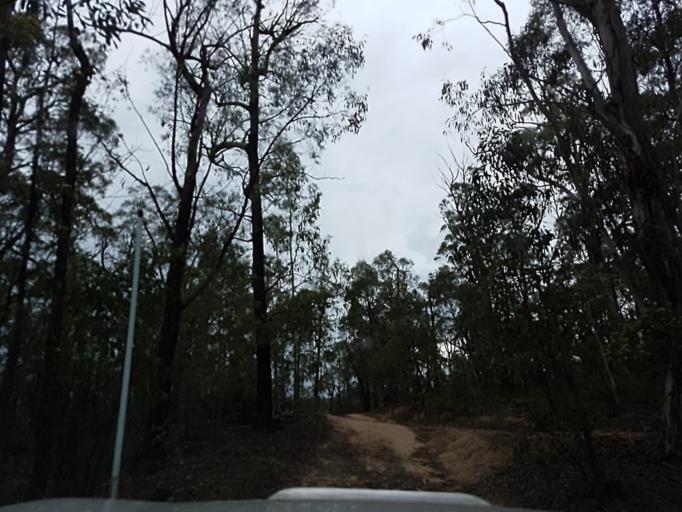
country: AU
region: New South Wales
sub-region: Snowy River
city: Jindabyne
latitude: -36.8553
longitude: 148.3334
